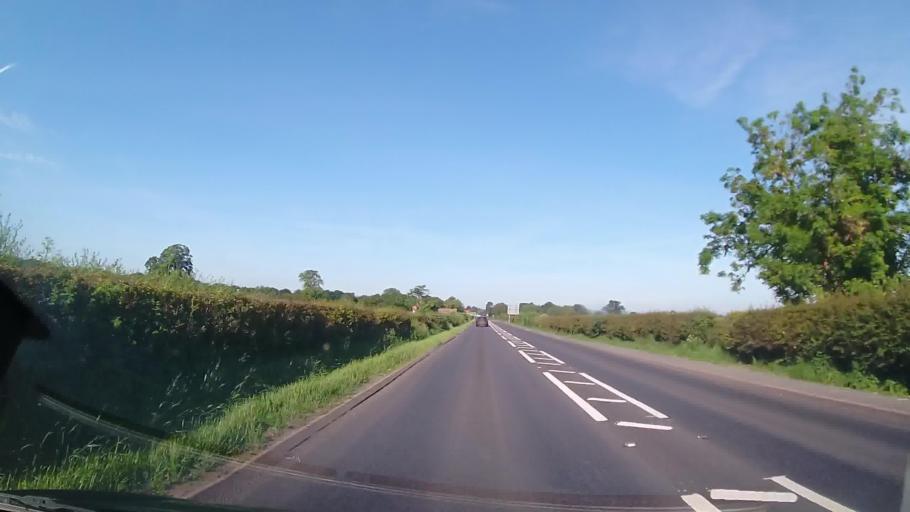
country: GB
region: England
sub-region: Shropshire
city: Ford
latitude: 52.7155
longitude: -2.8430
